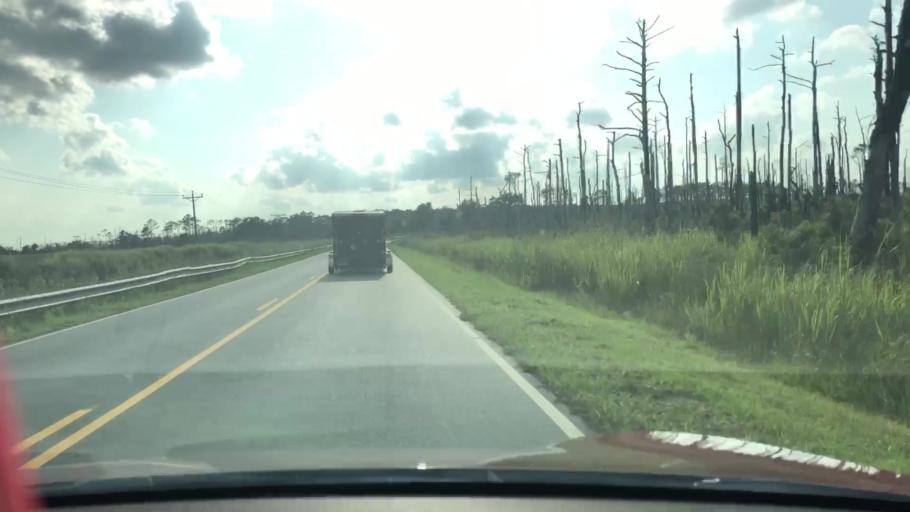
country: US
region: North Carolina
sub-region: Dare County
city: Wanchese
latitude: 35.6075
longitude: -75.8135
